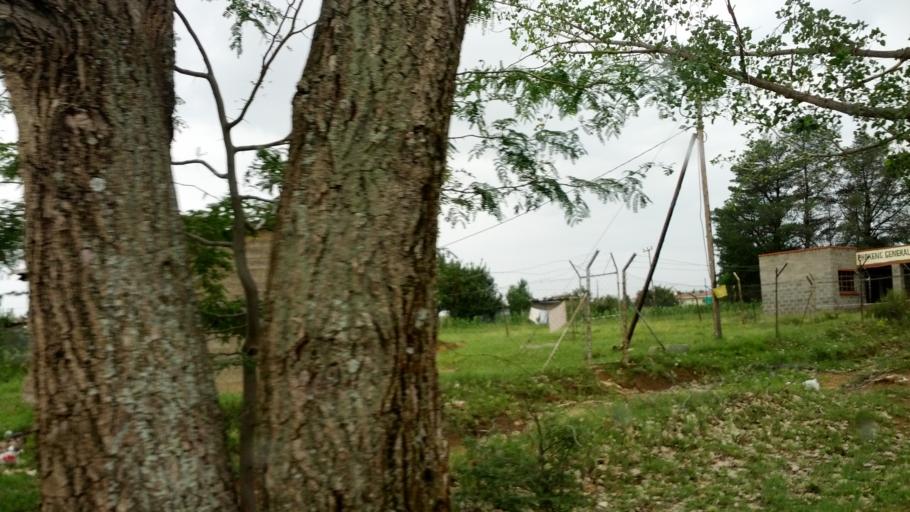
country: LS
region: Berea
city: Teyateyaneng
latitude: -29.1069
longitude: 27.9609
